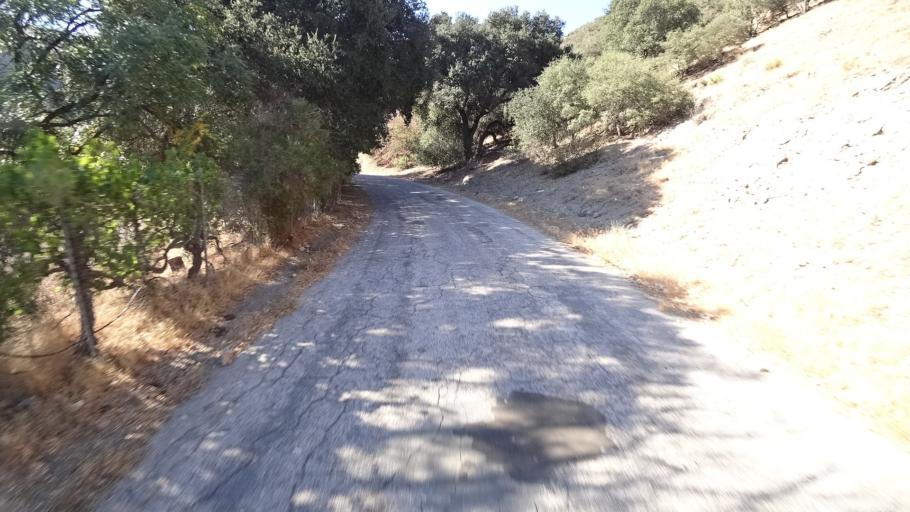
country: US
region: California
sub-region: Monterey County
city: Greenfield
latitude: 36.2105
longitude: -121.2798
